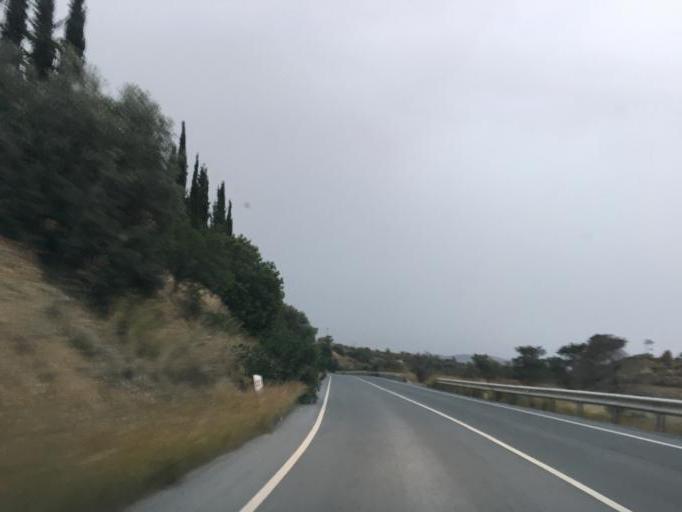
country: CY
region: Limassol
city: Parekklisha
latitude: 34.7766
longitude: 33.1612
